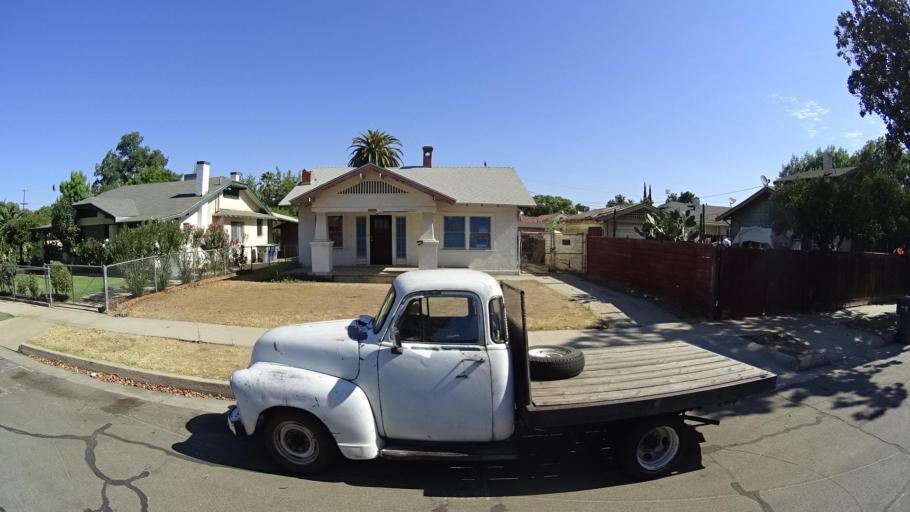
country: US
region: California
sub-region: Fresno County
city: Fresno
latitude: 36.7328
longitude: -119.7681
